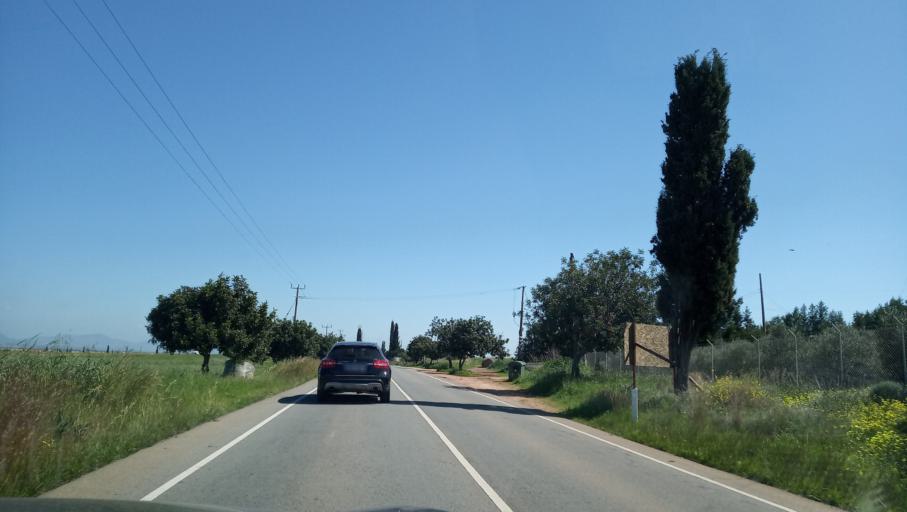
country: CY
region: Lefkosia
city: Astromeritis
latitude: 35.1153
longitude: 33.0006
